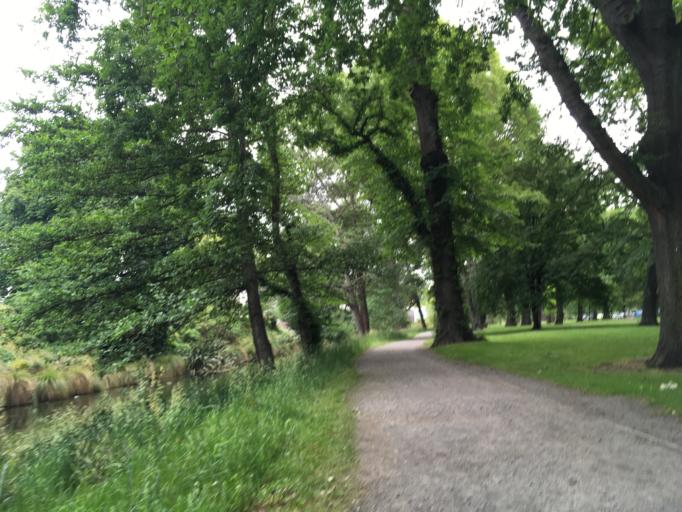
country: NZ
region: Canterbury
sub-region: Christchurch City
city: Christchurch
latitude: -43.5294
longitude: 172.6248
